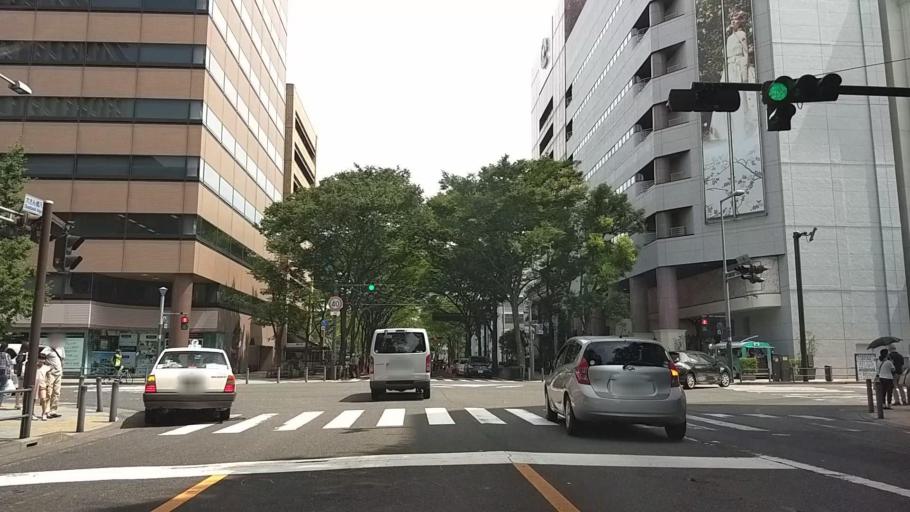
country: JP
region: Kanagawa
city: Yokohama
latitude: 35.4460
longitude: 139.6435
